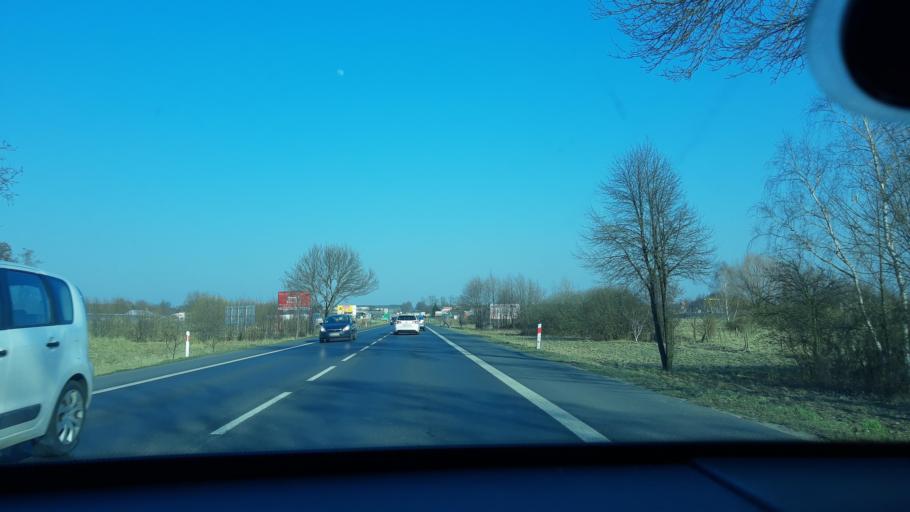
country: PL
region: Lodz Voivodeship
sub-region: Powiat sieradzki
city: Sieradz
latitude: 51.6006
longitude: 18.7774
